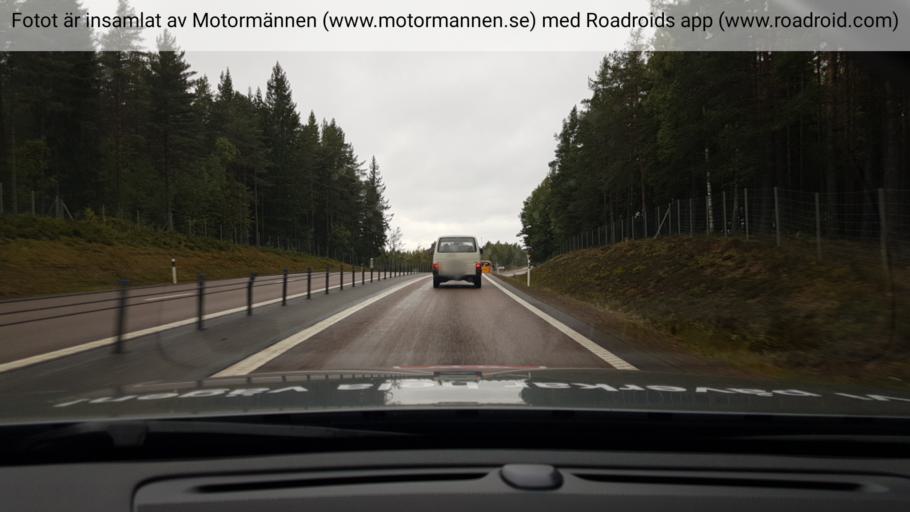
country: SE
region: Vaermland
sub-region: Kristinehamns Kommun
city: Kristinehamn
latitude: 59.3132
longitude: 14.1651
